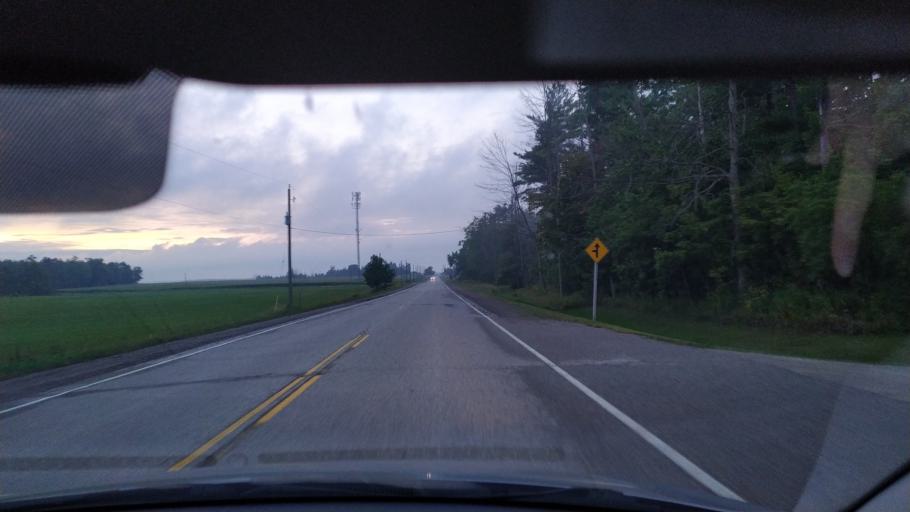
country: CA
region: Ontario
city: Kitchener
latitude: 43.3591
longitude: -80.7054
